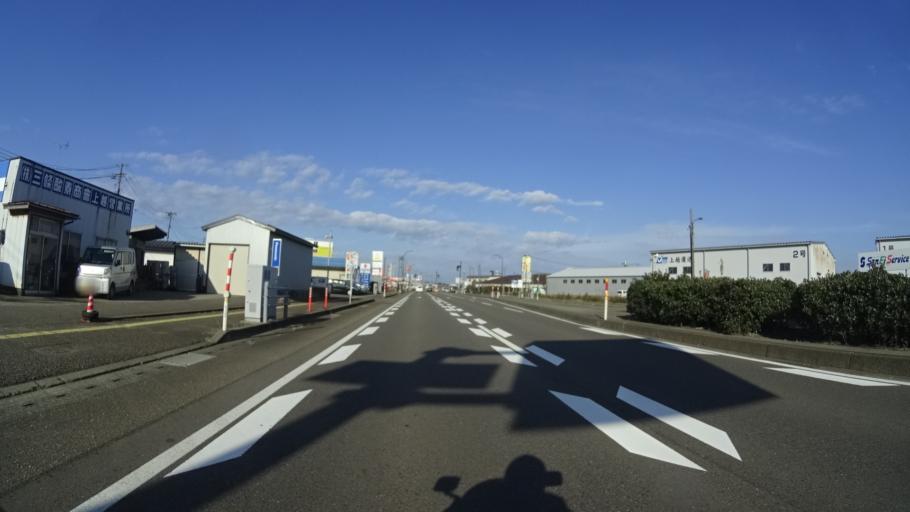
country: JP
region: Niigata
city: Joetsu
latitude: 37.1835
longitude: 138.2711
